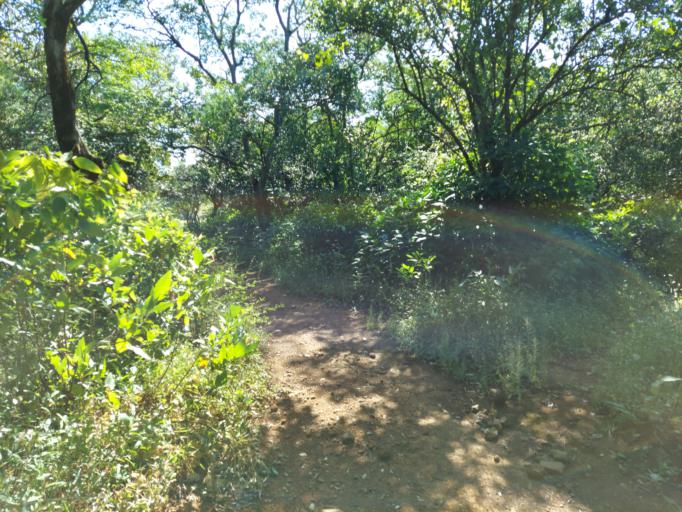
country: IN
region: Maharashtra
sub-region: Sindhudurg
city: Kudal
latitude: 16.0817
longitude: 73.8473
